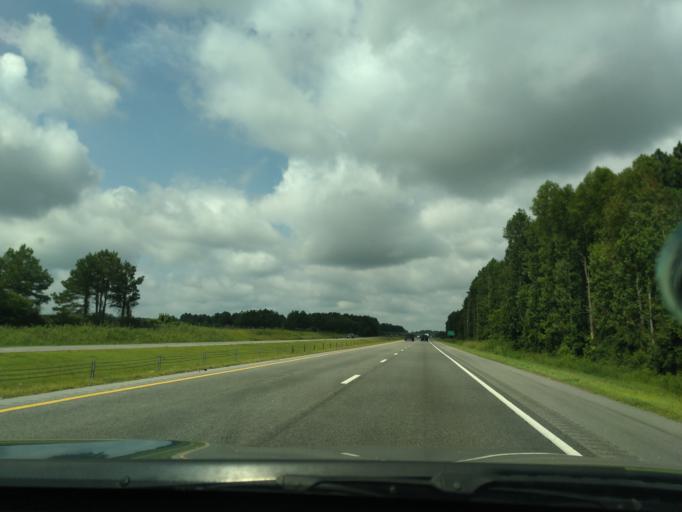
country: US
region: North Carolina
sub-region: Martin County
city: Robersonville
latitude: 35.8428
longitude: -77.2219
